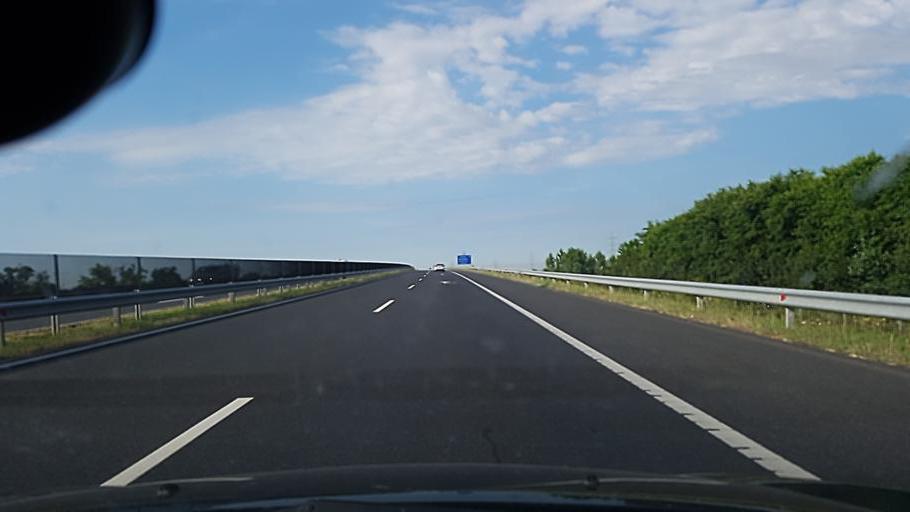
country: HU
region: Fejer
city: Ivancsa
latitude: 47.1807
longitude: 18.8078
